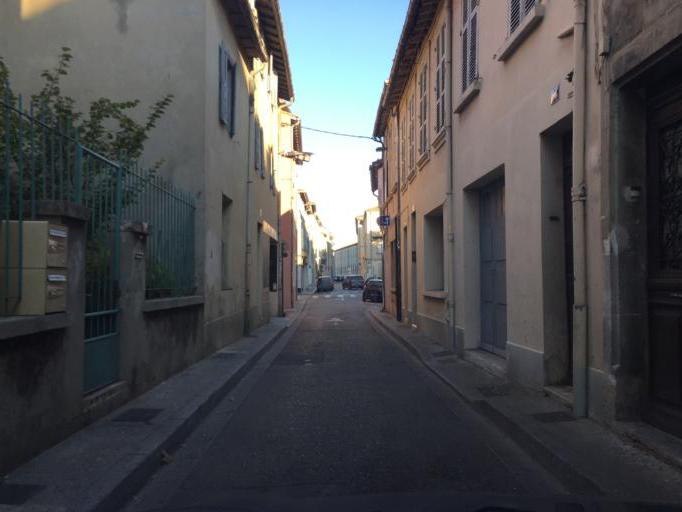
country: FR
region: Provence-Alpes-Cote d'Azur
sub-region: Departement du Vaucluse
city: Avignon
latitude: 43.9494
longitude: 4.8138
